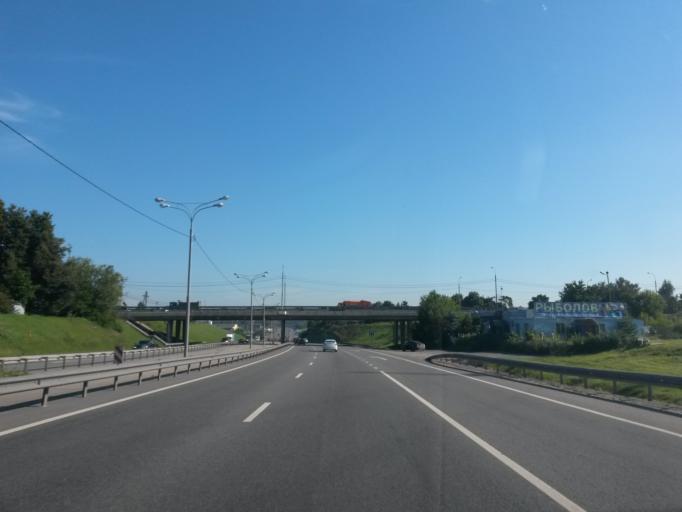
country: RU
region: Moskovskaya
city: Lesnyye Polyany
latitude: 55.9853
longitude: 37.8709
